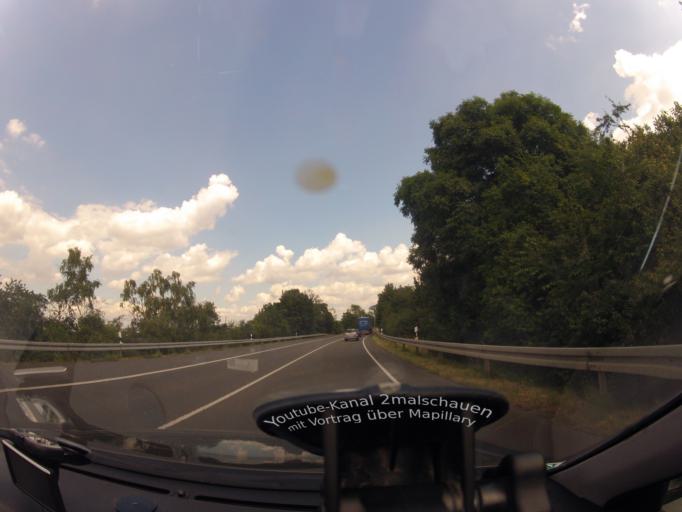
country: DE
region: Saxony
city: Doberschutz
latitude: 51.4873
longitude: 12.7300
